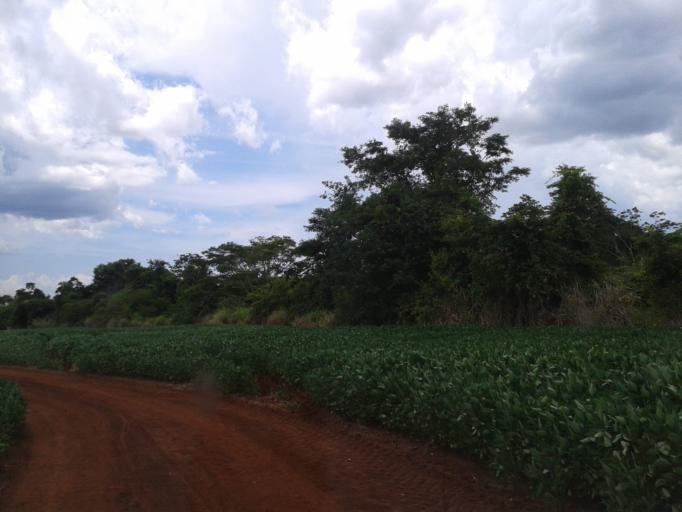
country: BR
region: Minas Gerais
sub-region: Centralina
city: Centralina
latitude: -18.6805
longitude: -49.2168
